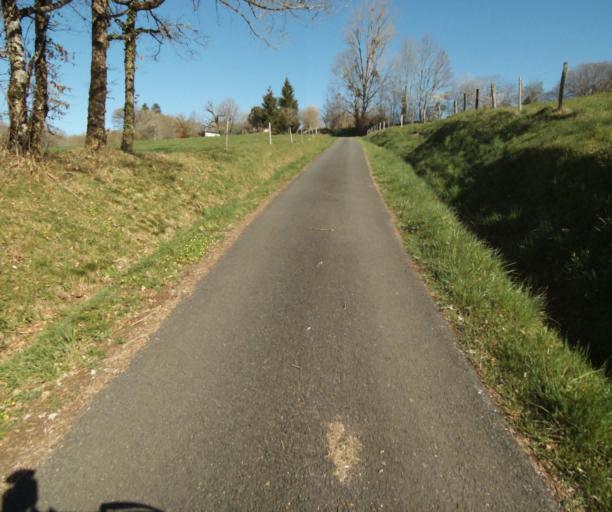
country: FR
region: Limousin
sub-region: Departement de la Correze
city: Seilhac
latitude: 45.3843
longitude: 1.7511
